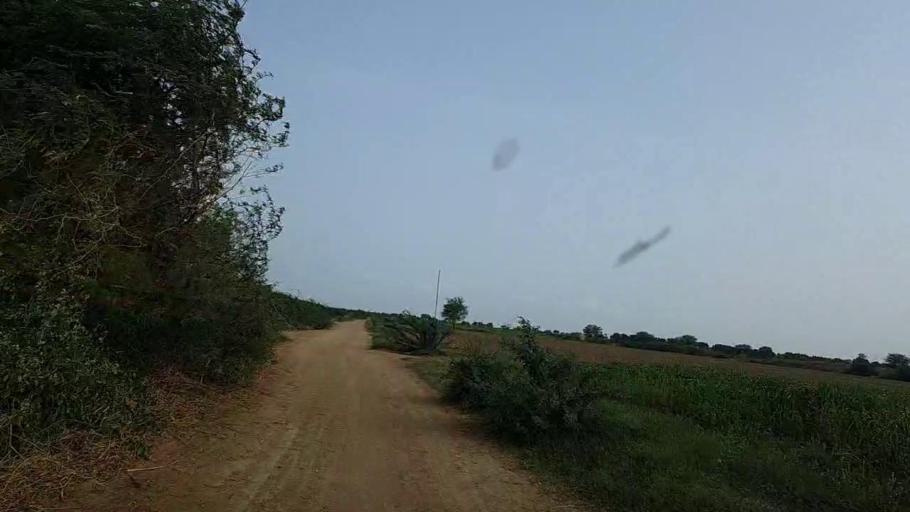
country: PK
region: Sindh
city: Kotri
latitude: 25.2434
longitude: 68.2421
